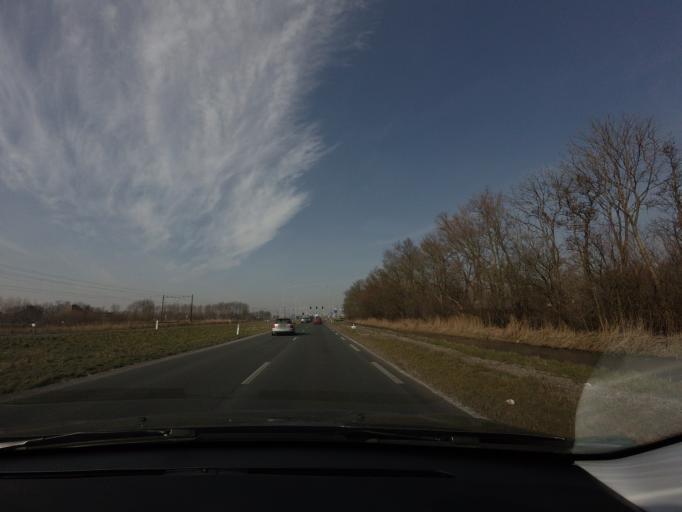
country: NL
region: North Holland
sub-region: Gemeente Uitgeest
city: Uitgeest
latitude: 52.5006
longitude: 4.7432
